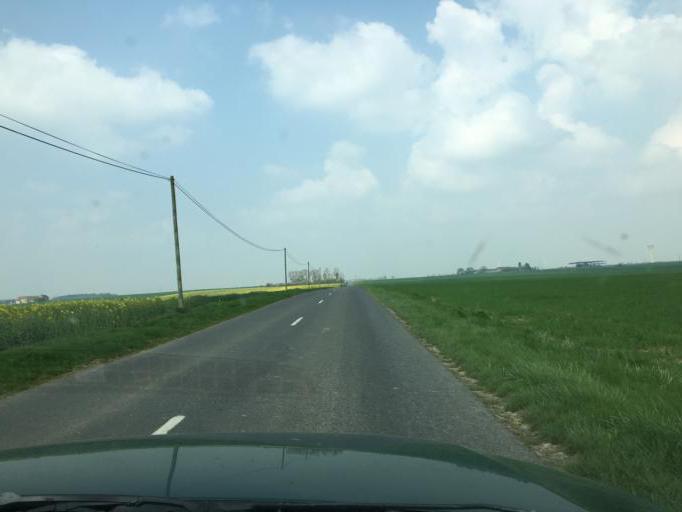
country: FR
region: Centre
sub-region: Departement du Loir-et-Cher
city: Ouzouer-le-Marche
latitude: 47.8479
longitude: 1.5301
